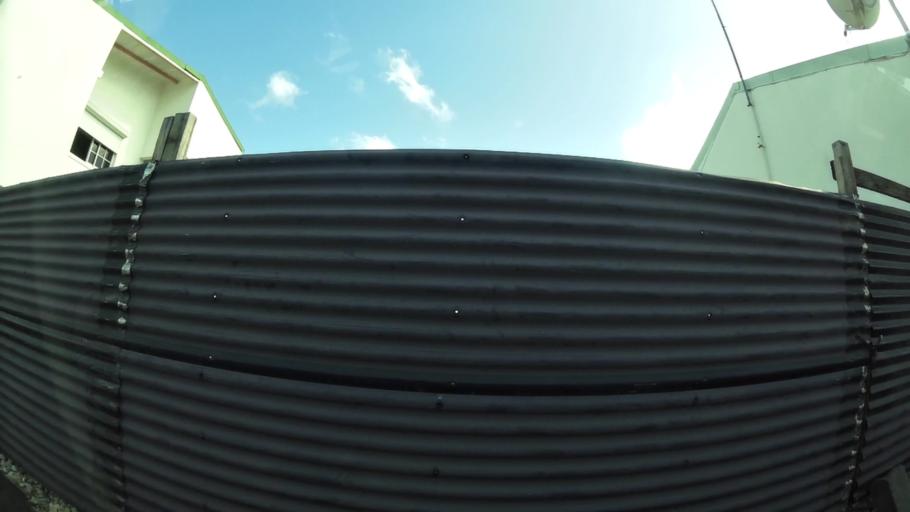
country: GP
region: Guadeloupe
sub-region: Guadeloupe
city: Port-Louis
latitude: 16.4186
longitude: -61.5334
